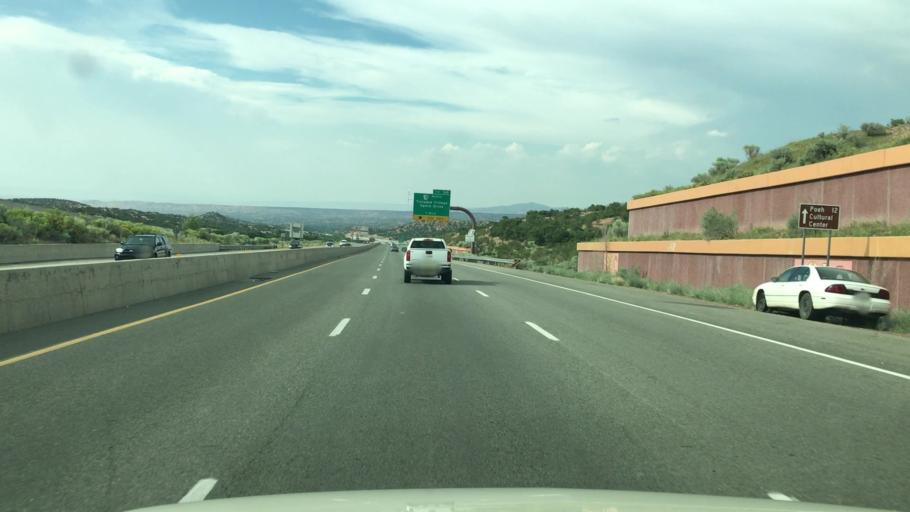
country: US
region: New Mexico
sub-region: Santa Fe County
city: Santa Fe
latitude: 35.7247
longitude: -105.9319
